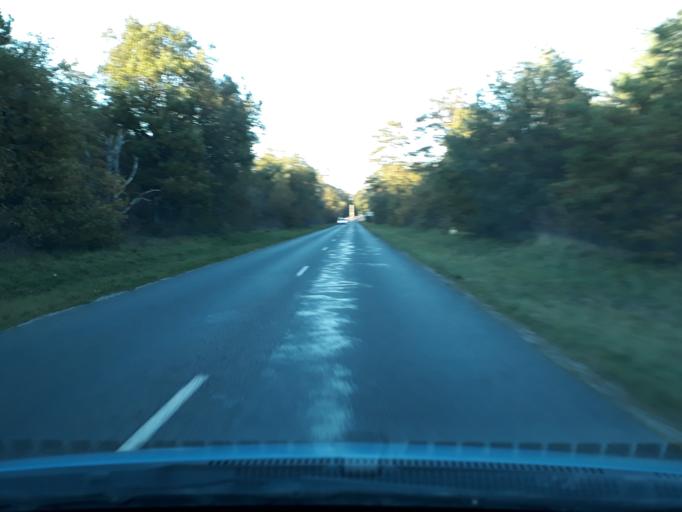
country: FR
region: Ile-de-France
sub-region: Departement de Seine-et-Marne
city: Bois-le-Roi
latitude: 48.4400
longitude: 2.7165
